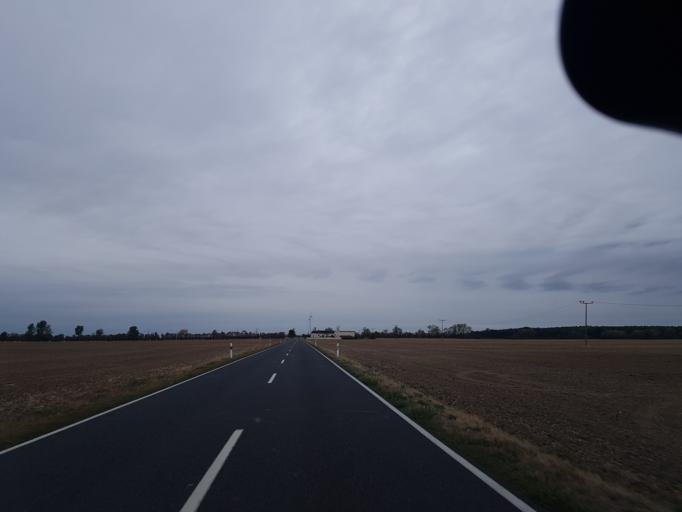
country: DE
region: Saxony-Anhalt
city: Prettin
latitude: 51.6742
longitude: 12.9121
